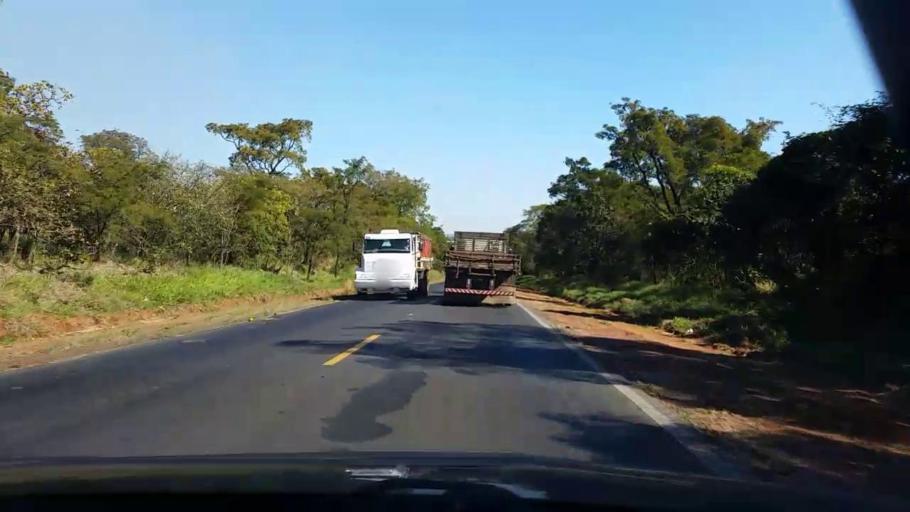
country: BR
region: Sao Paulo
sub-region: Sao Manuel
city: Sao Manuel
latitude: -22.7946
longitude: -48.6584
